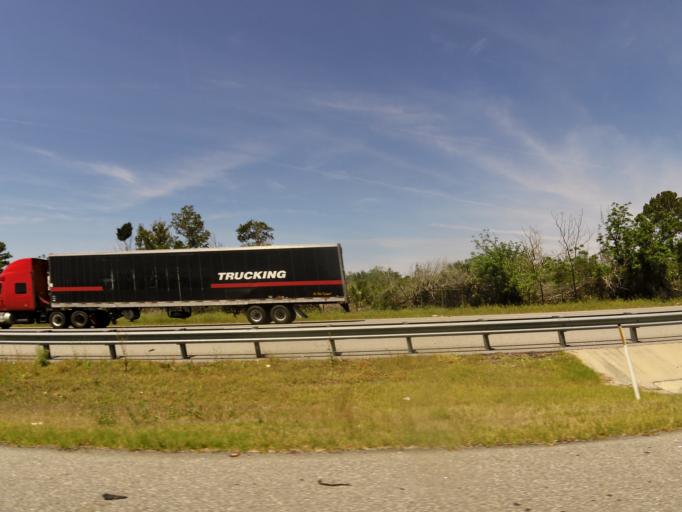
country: US
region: Georgia
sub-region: Glynn County
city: Dock Junction
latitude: 31.2023
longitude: -81.5362
